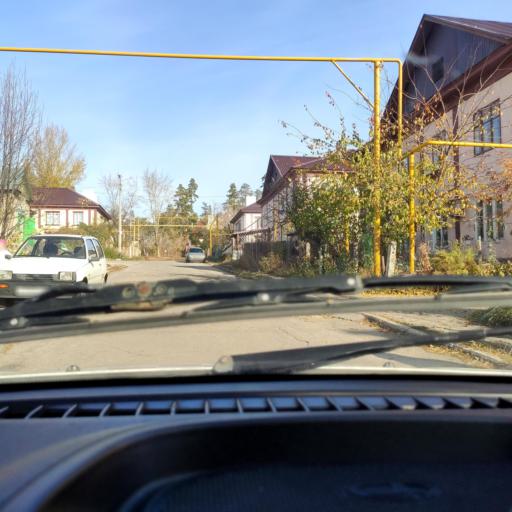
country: RU
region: Samara
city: Tol'yatti
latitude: 53.4751
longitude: 49.3707
